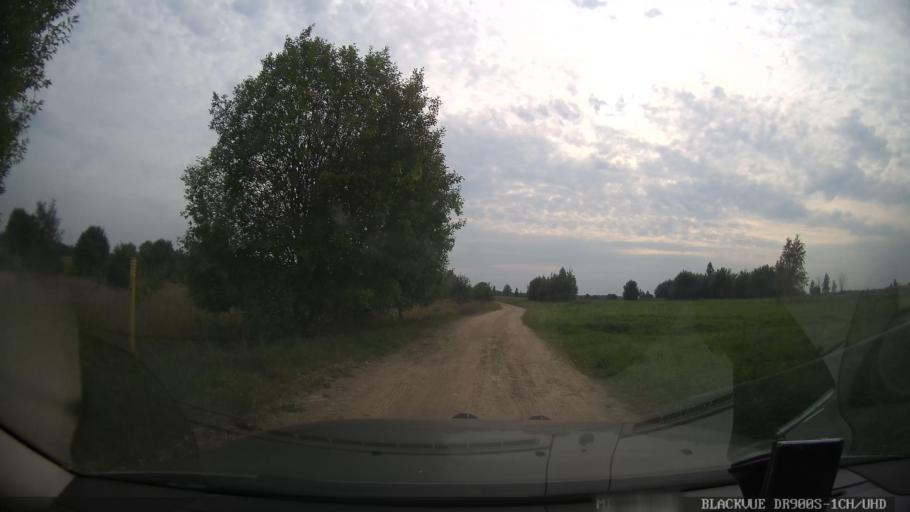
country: BY
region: Grodnenskaya
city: Ashmyany
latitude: 54.5346
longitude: 25.6728
